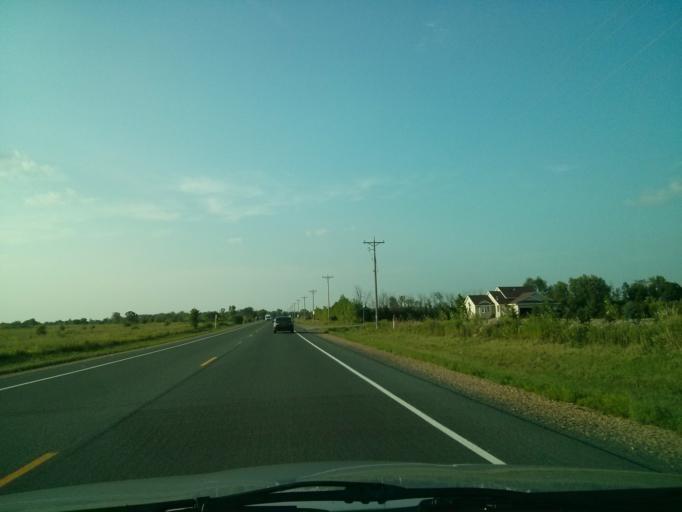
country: US
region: Wisconsin
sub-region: Saint Croix County
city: North Hudson
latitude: 45.0082
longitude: -92.6754
